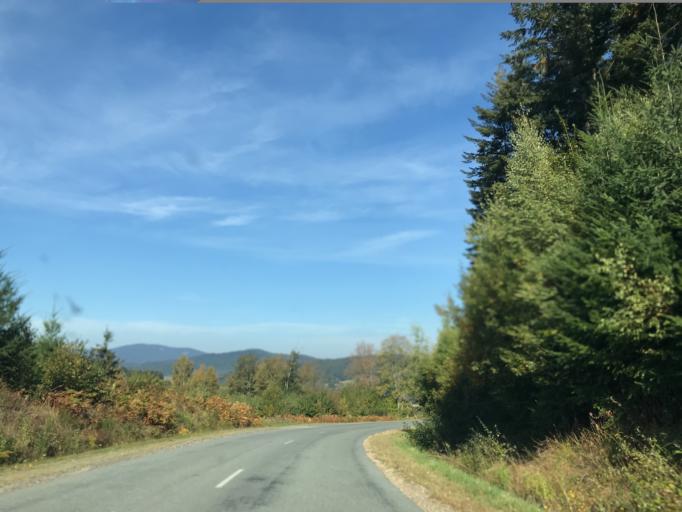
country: FR
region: Rhone-Alpes
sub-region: Departement de la Loire
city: Noiretable
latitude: 45.8113
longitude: 3.7473
